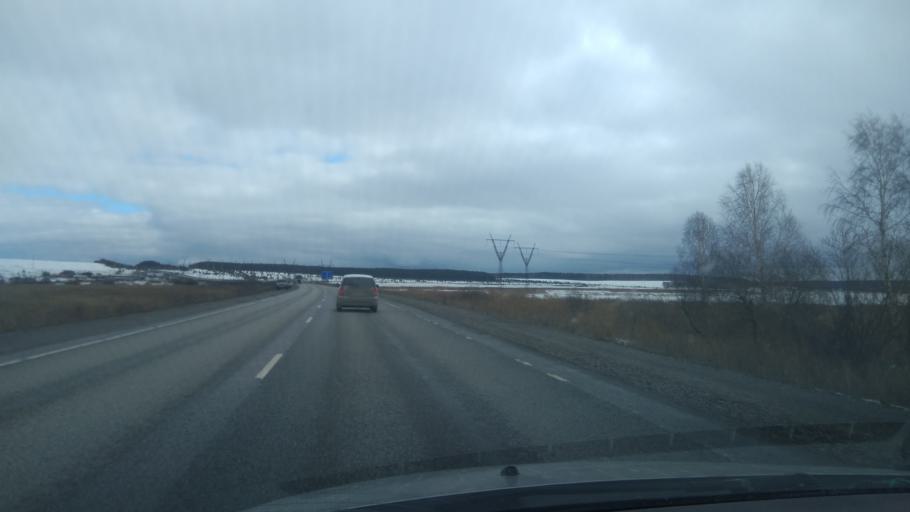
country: RU
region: Sverdlovsk
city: Achit
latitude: 56.7849
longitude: 57.8924
